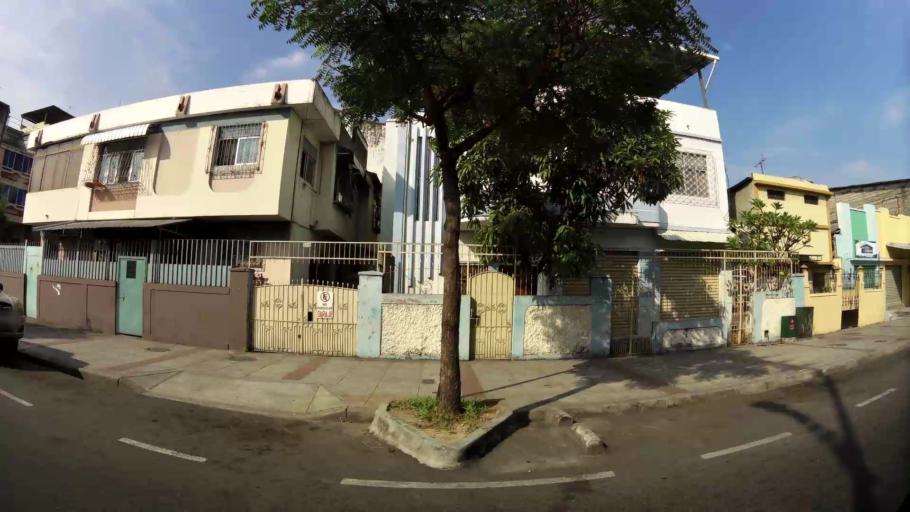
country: EC
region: Guayas
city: Guayaquil
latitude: -2.1941
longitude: -79.8955
